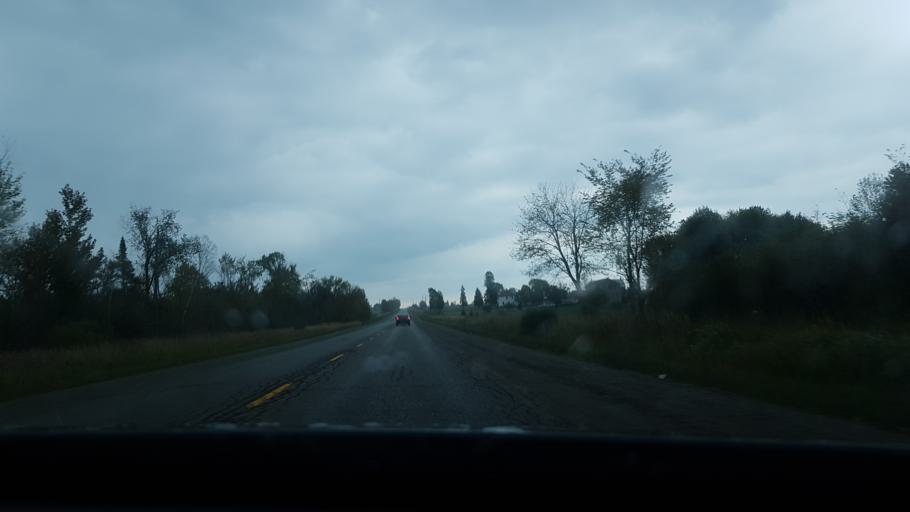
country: CA
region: Ontario
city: Omemee
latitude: 44.3778
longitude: -78.6263
